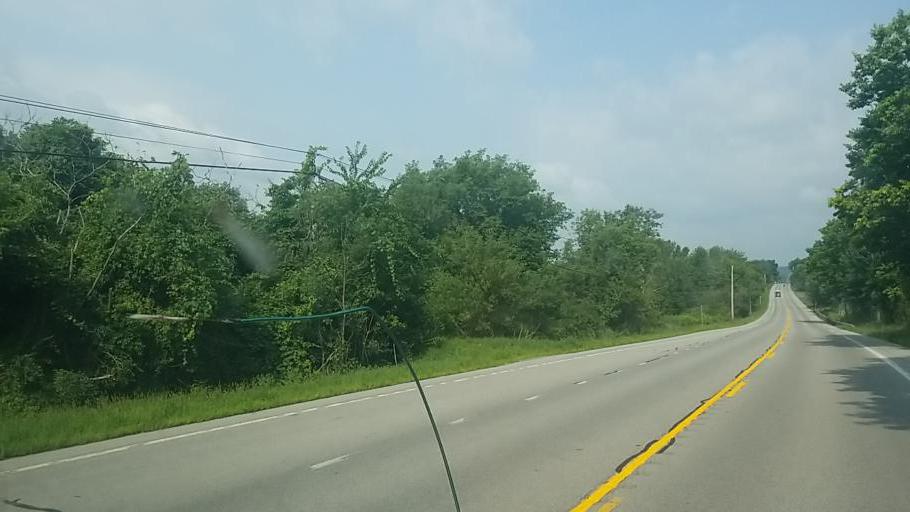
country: US
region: New York
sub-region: Montgomery County
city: Saint Johnsville
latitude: 42.9817
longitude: -74.6423
